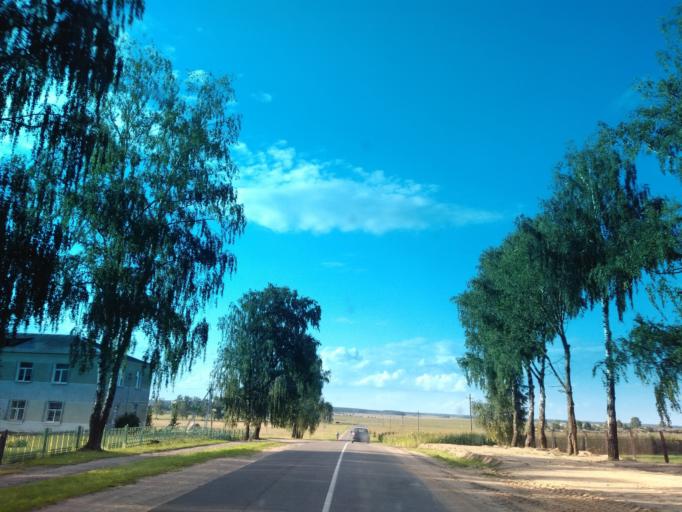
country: BY
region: Minsk
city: Kapyl'
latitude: 53.2632
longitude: 26.9574
